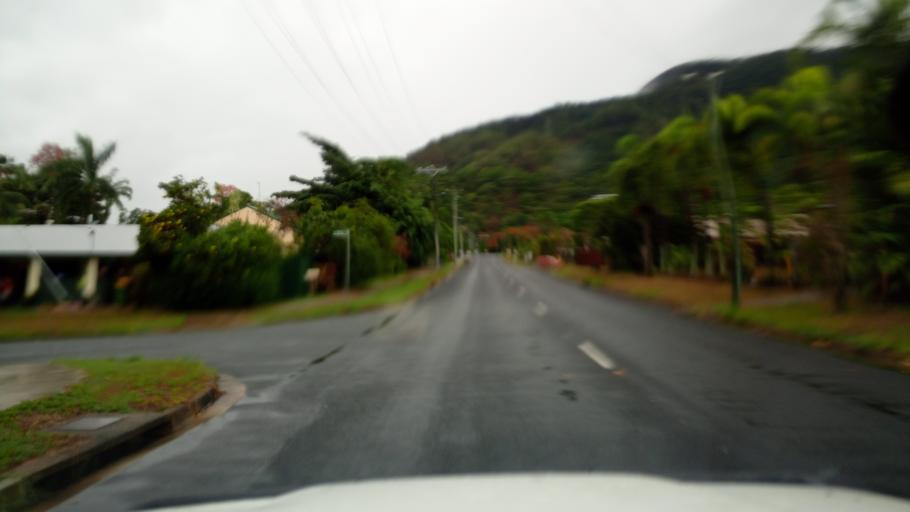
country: AU
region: Queensland
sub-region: Cairns
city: Woree
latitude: -16.9618
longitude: 145.7306
